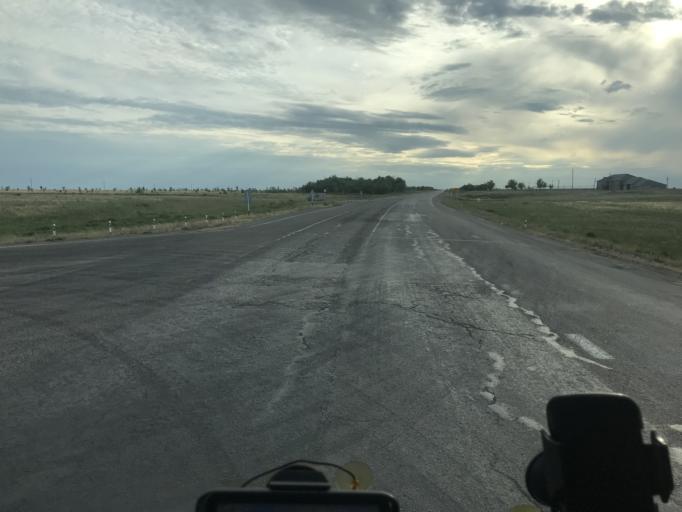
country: KZ
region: Aqtoebe
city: Martuk
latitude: 50.2073
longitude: 56.4678
